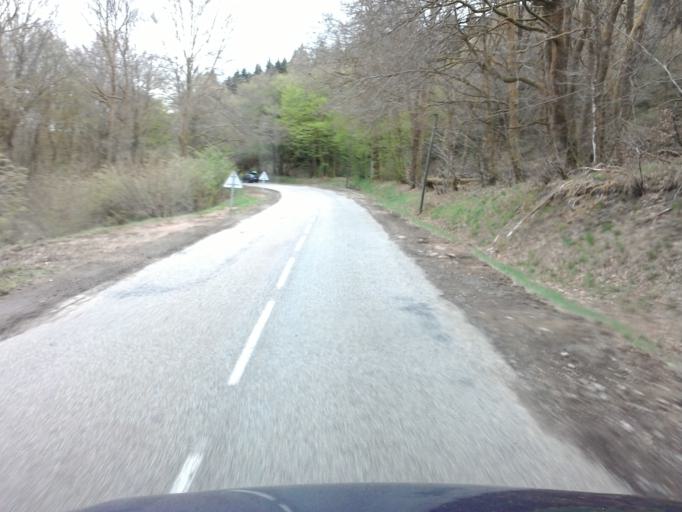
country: FR
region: Bourgogne
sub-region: Departement de la Cote-d'Or
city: Saulieu
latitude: 47.2466
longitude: 4.0464
